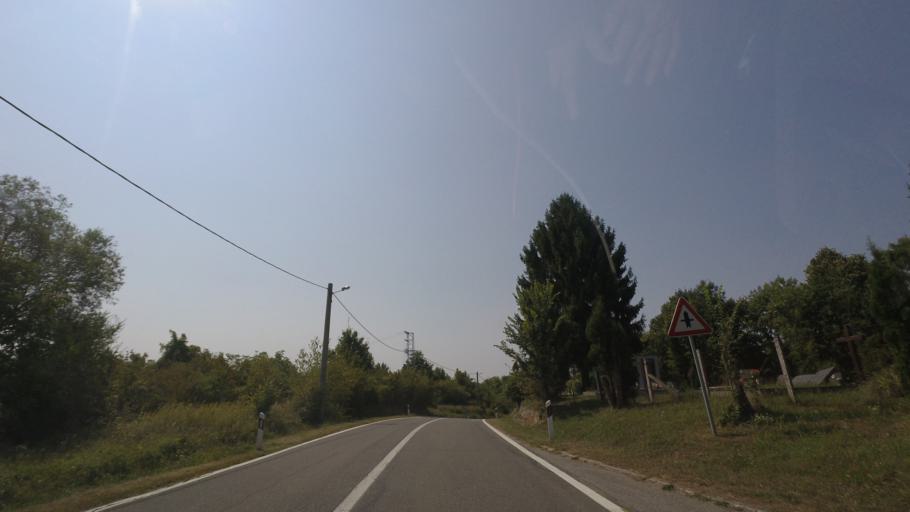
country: HR
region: Pozesko-Slavonska
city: Lipik
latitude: 45.4159
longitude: 17.0804
